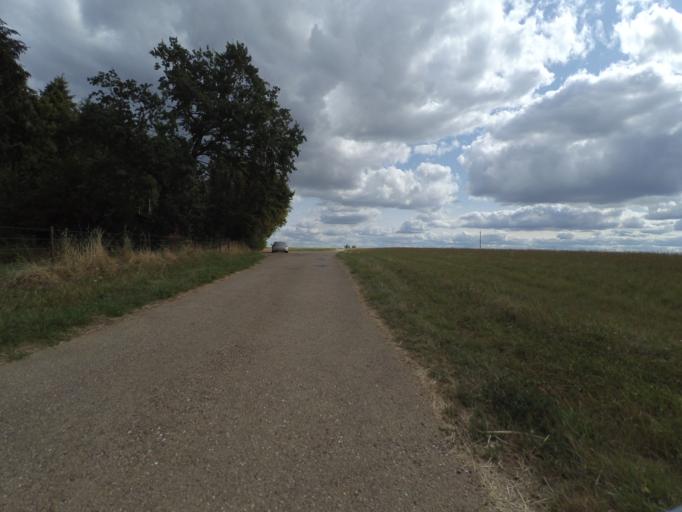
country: LU
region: Grevenmacher
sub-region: Canton de Remich
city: Waldbredimus
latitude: 49.5309
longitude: 6.2838
